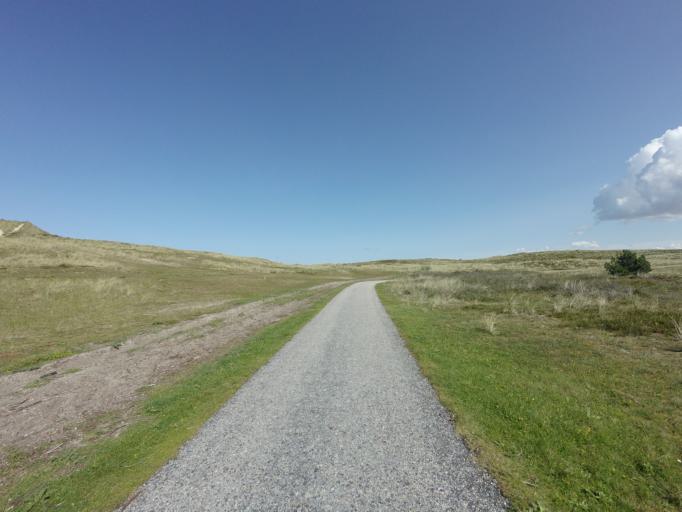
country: NL
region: Friesland
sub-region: Gemeente Terschelling
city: West-Terschelling
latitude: 53.4147
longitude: 5.3581
